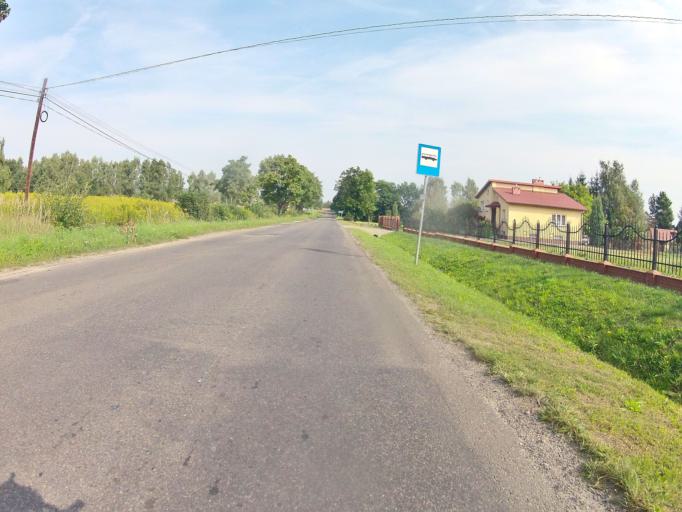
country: PL
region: Subcarpathian Voivodeship
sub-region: Powiat jasielski
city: Kolaczyce
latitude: 49.7829
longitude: 21.4042
